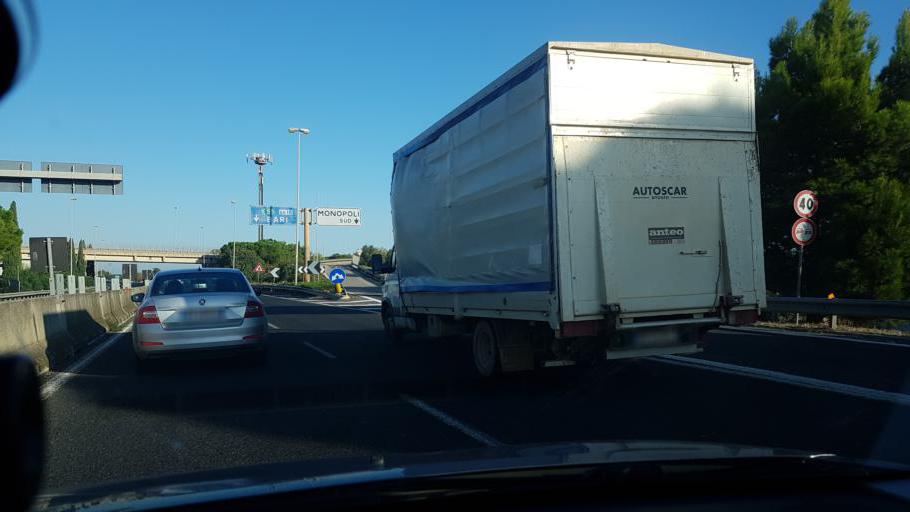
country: IT
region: Apulia
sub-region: Provincia di Bari
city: Monopoli
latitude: 40.9205
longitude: 17.3170
